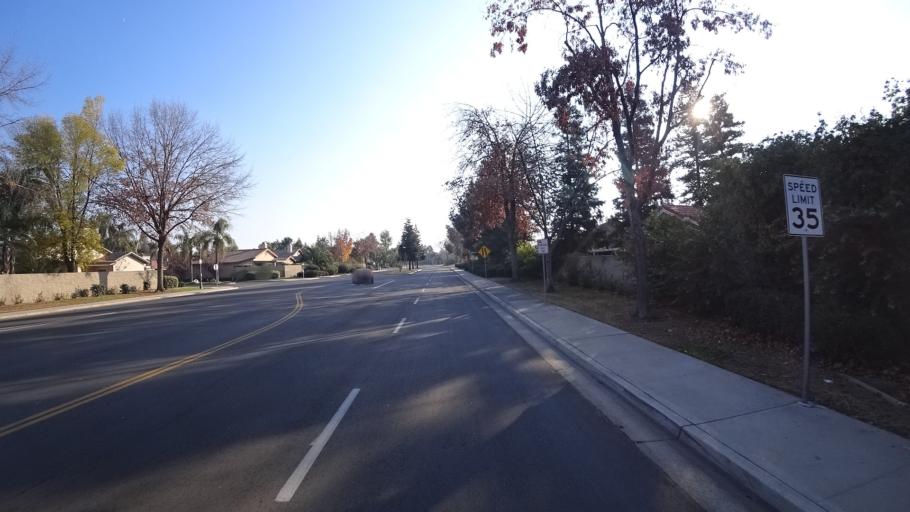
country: US
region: California
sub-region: Kern County
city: Greenacres
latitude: 35.3393
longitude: -119.1012
